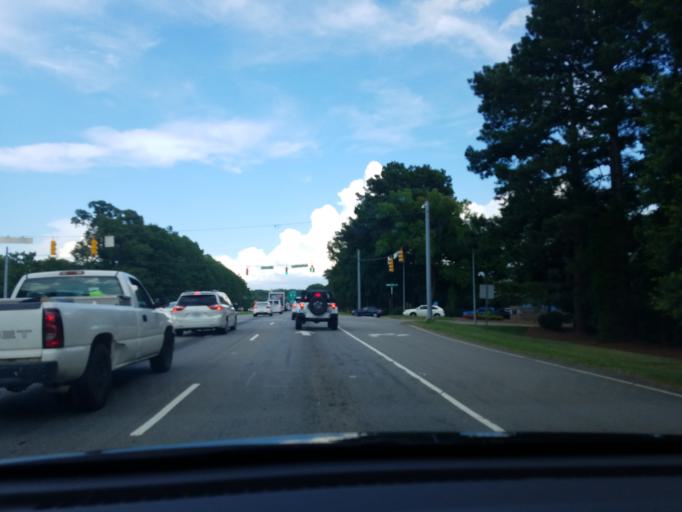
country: US
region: North Carolina
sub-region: Wake County
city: Apex
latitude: 35.7389
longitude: -78.7991
